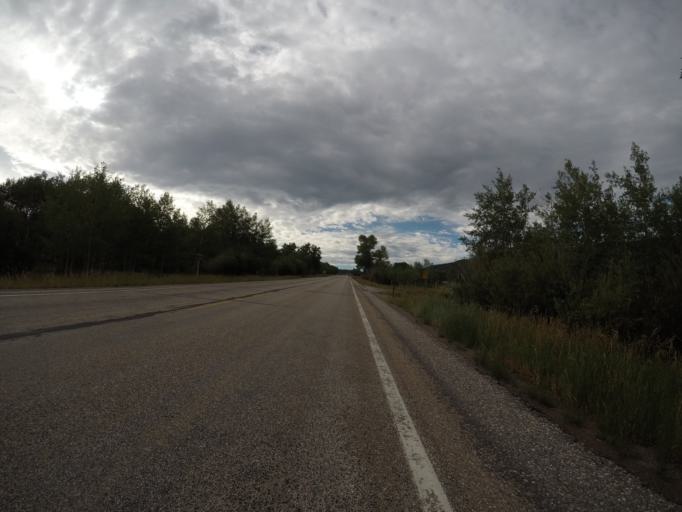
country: US
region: Wyoming
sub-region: Carbon County
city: Saratoga
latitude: 41.3561
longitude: -106.5385
